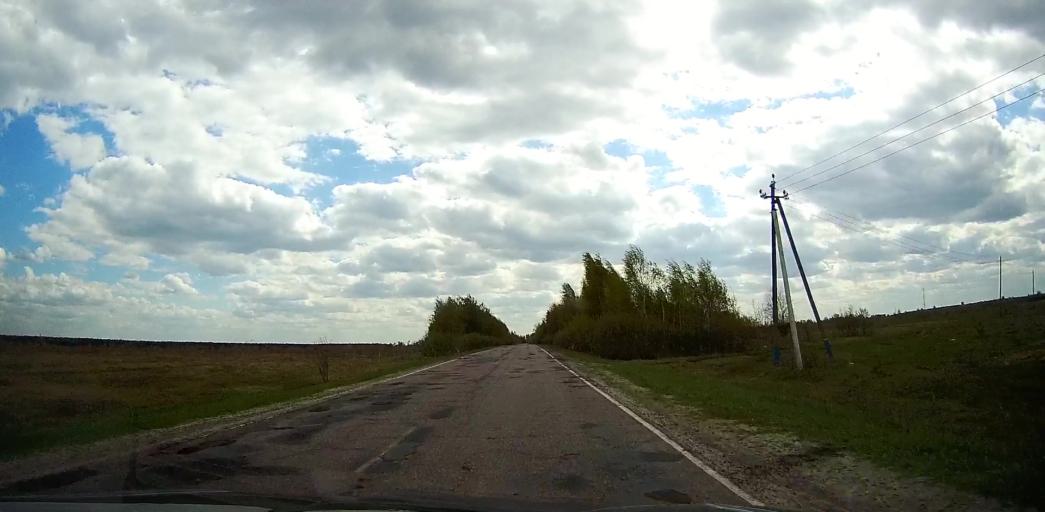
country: RU
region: Moskovskaya
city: Davydovo
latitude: 55.6385
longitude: 38.7480
